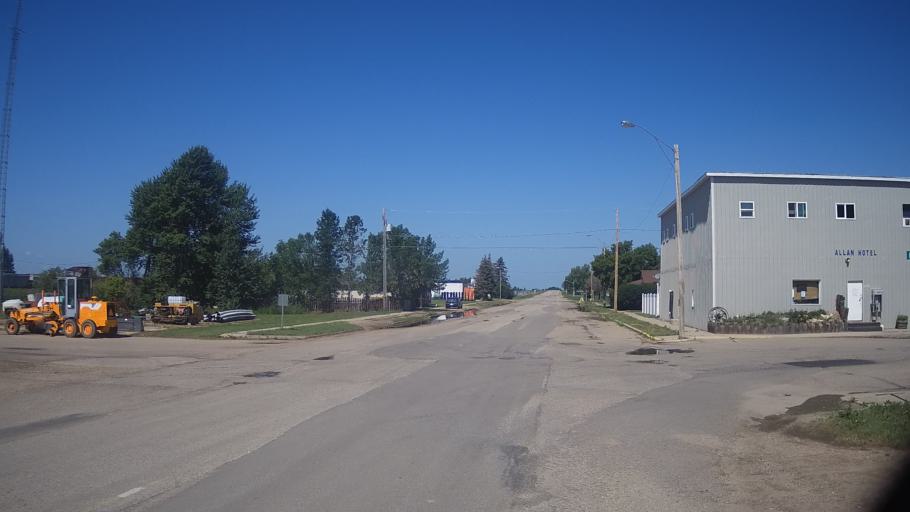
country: CA
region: Saskatchewan
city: Saskatoon
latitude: 51.8930
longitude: -106.0561
